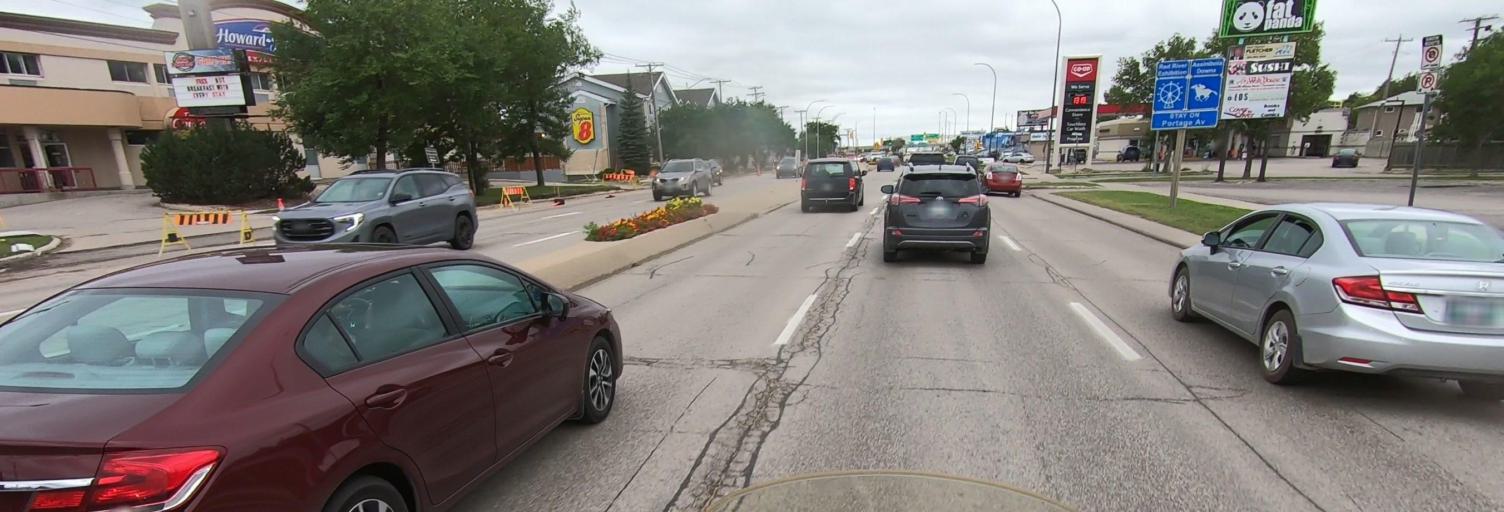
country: CA
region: Manitoba
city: Headingley
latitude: 49.8816
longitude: -97.3173
